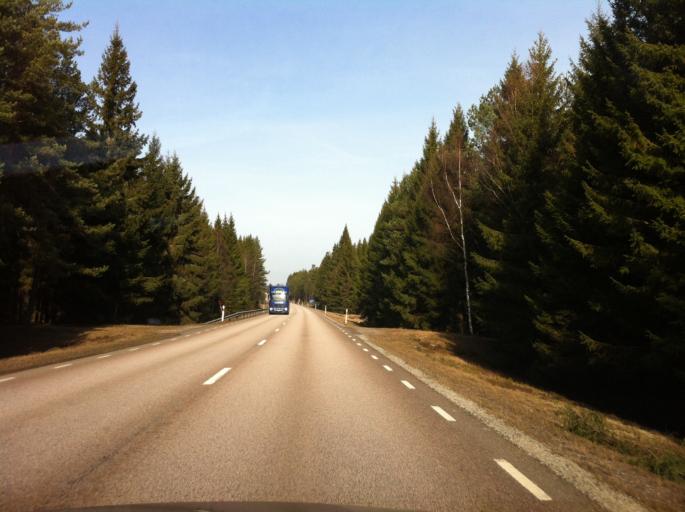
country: SE
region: Joenkoeping
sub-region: Mullsjo Kommun
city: Mullsjoe
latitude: 58.0582
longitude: 13.8568
